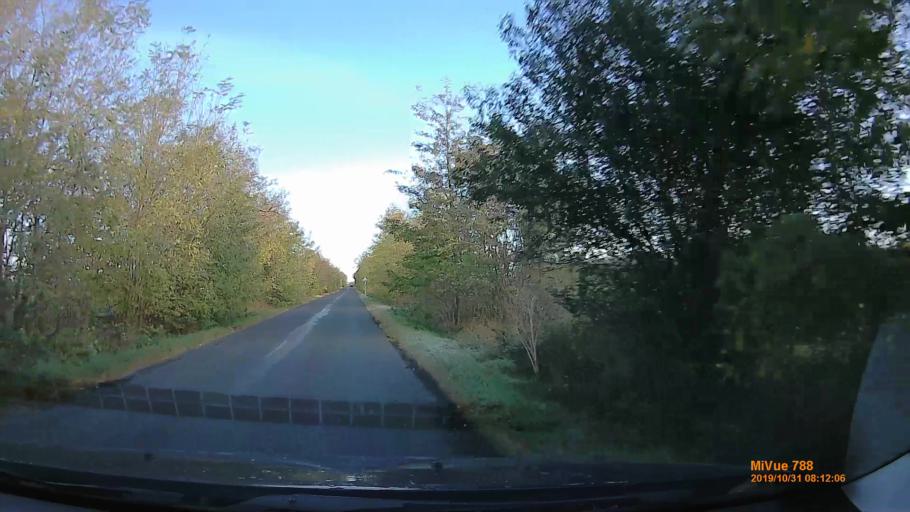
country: HU
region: Pest
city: Pilis
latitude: 47.3213
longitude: 19.5656
